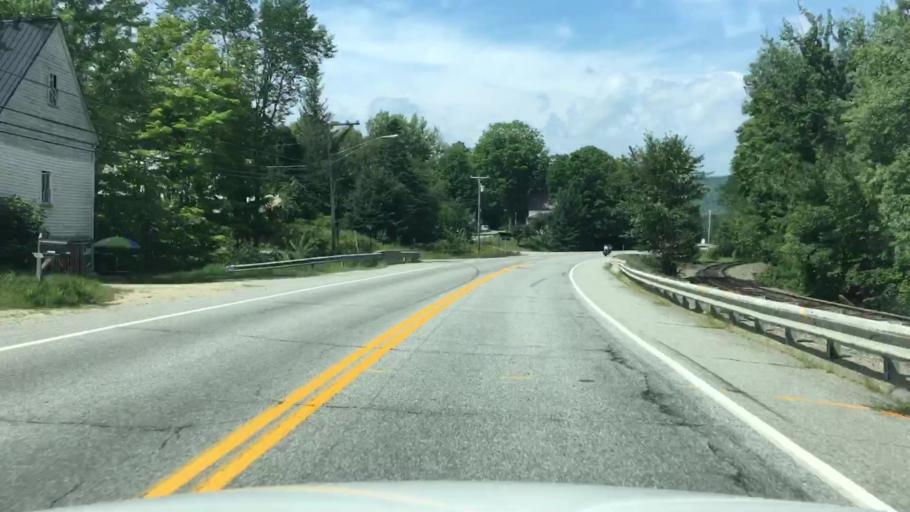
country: US
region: Maine
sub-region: Oxford County
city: Peru
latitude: 44.5057
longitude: -70.4042
